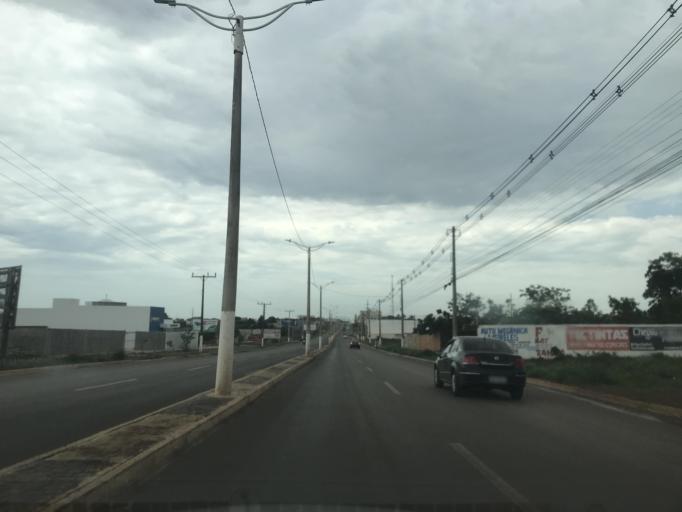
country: BR
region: Goias
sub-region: Luziania
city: Luziania
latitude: -16.2294
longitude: -47.9392
